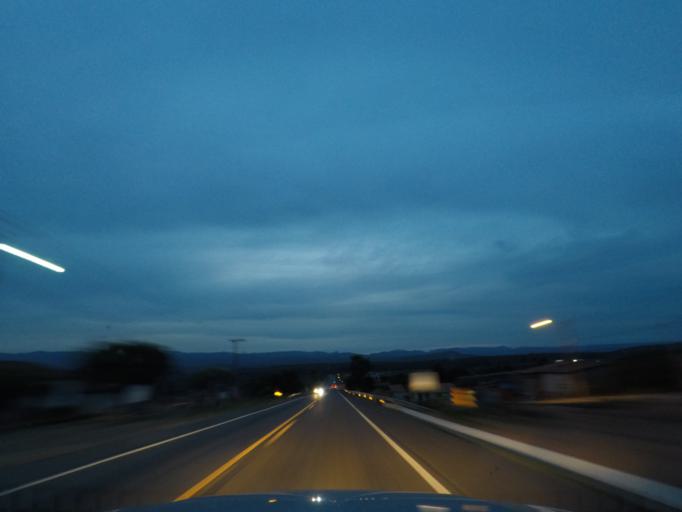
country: BR
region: Bahia
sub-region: Andarai
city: Vera Cruz
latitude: -12.4973
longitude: -41.2968
